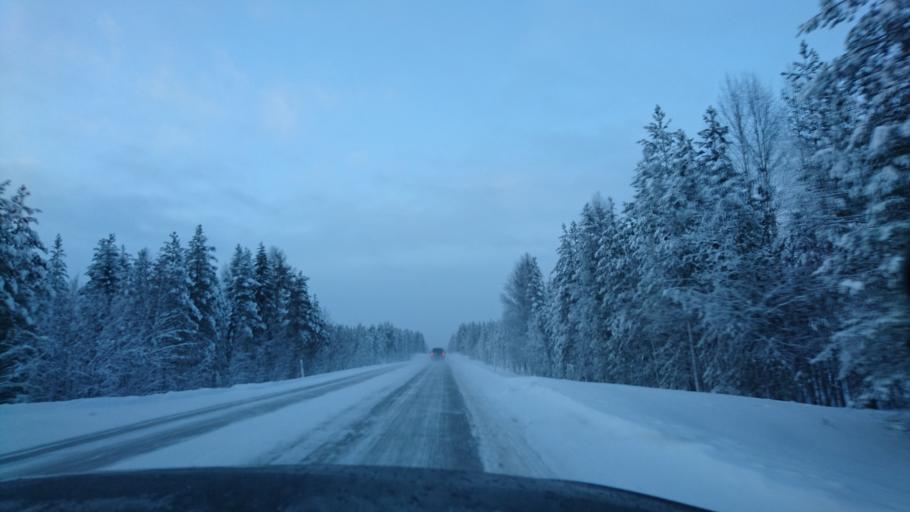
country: FI
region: Northern Ostrobothnia
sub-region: Koillismaa
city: Taivalkoski
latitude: 65.4682
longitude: 27.6804
